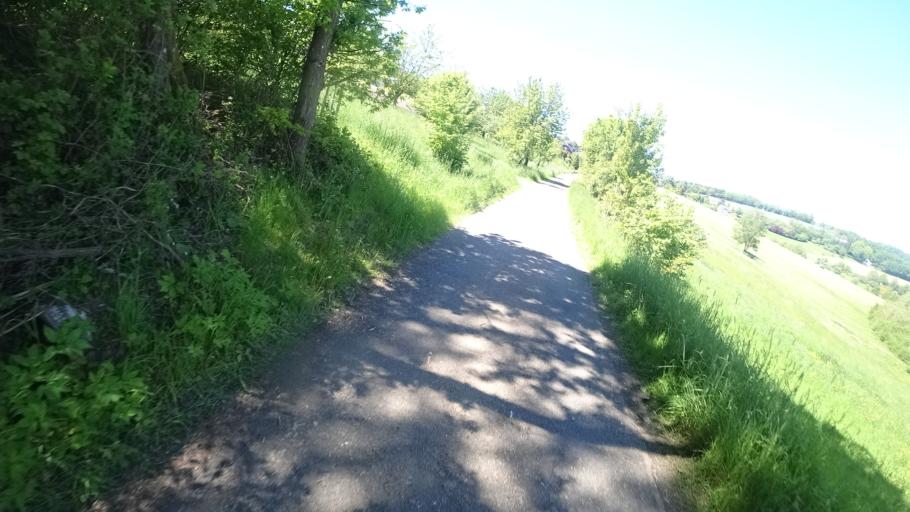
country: DE
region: Rheinland-Pfalz
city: Alsdorf
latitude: 50.7590
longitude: 7.8585
